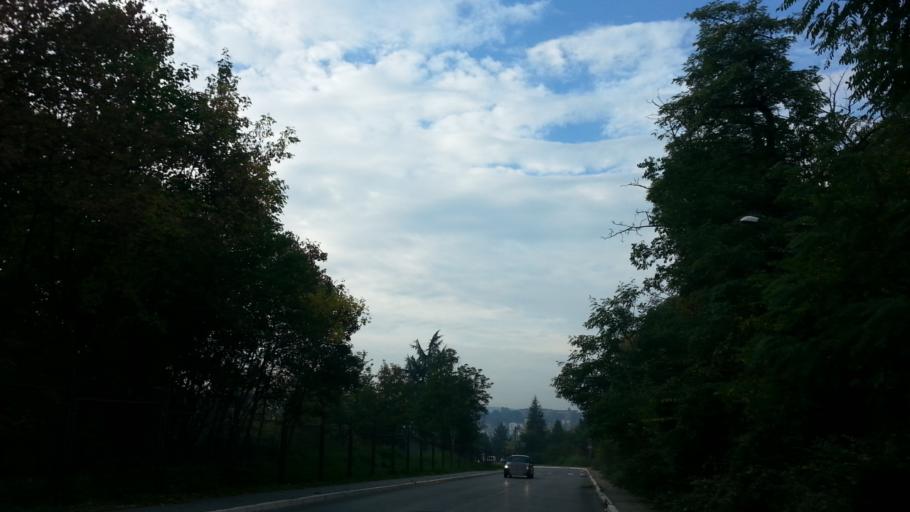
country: RS
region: Central Serbia
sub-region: Belgrade
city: Savski Venac
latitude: 44.7614
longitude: 20.4569
